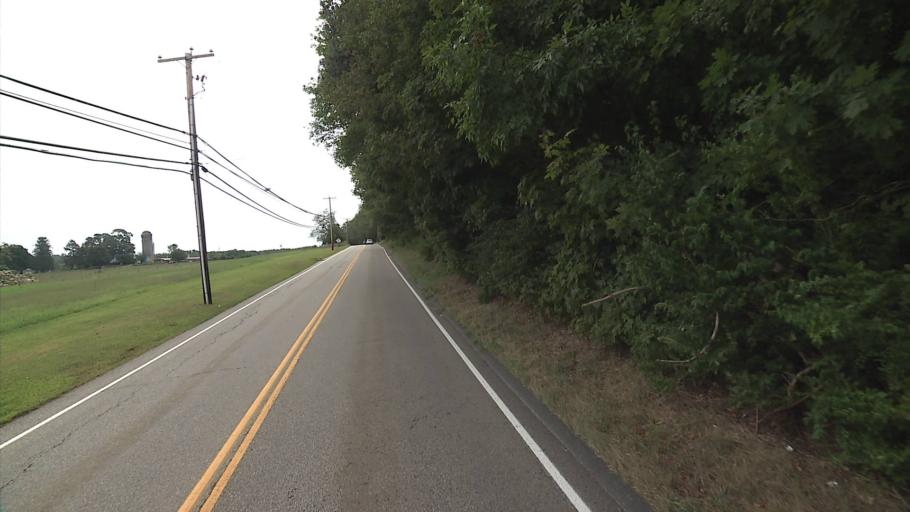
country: US
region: Connecticut
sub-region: Middlesex County
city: Essex Village
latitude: 41.3803
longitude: -72.3497
